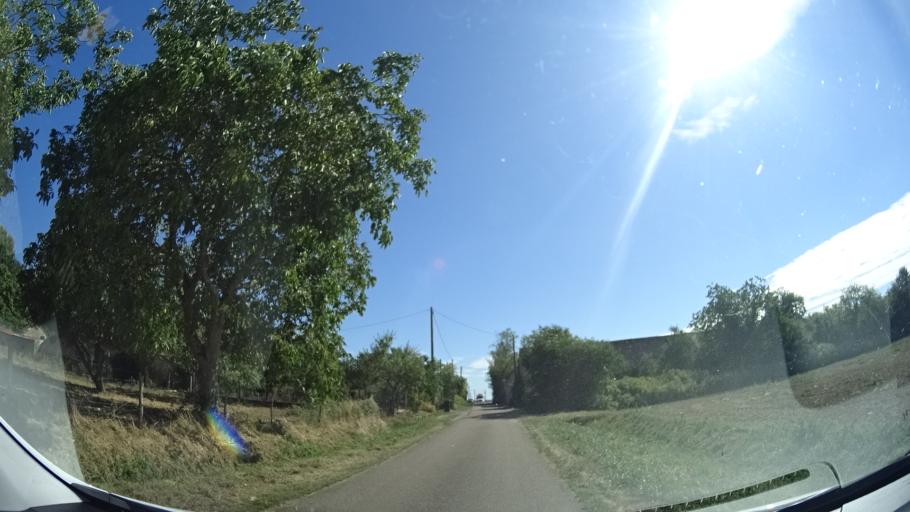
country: FR
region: Centre
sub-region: Departement du Loiret
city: Trigueres
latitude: 47.9495
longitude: 2.9623
